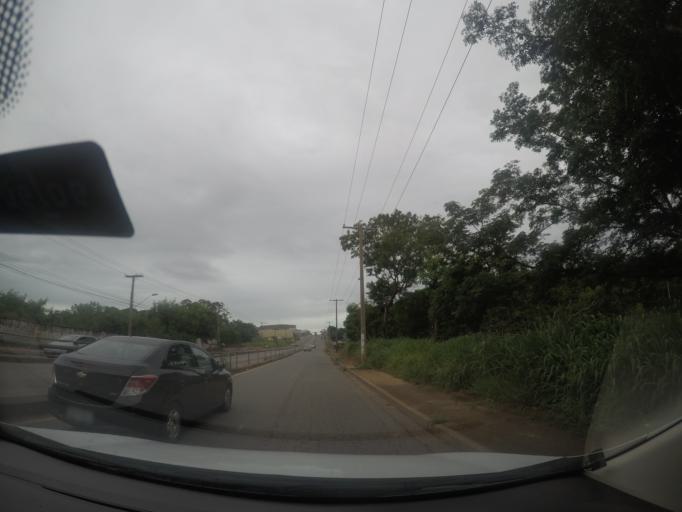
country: BR
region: Goias
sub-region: Goiania
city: Goiania
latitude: -16.6653
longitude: -49.3165
